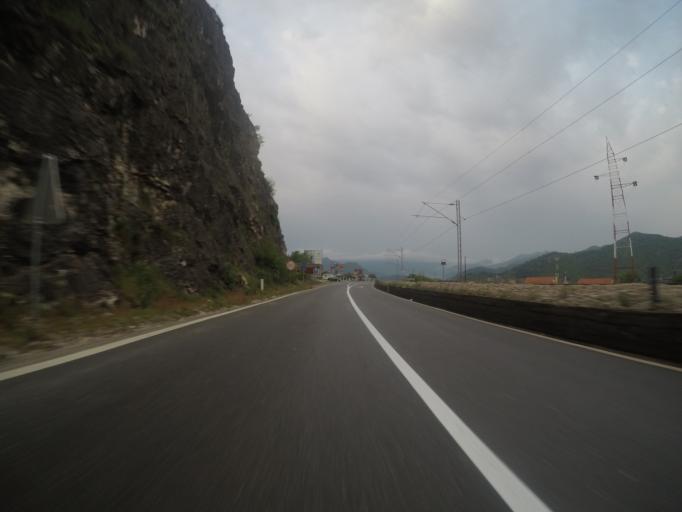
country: ME
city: Mojanovici
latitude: 42.2737
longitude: 19.1242
